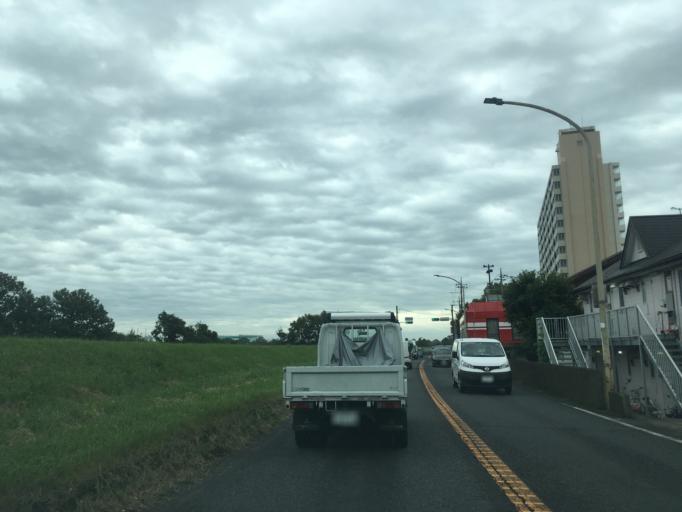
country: JP
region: Tokyo
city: Chofugaoka
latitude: 35.6328
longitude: 139.5588
